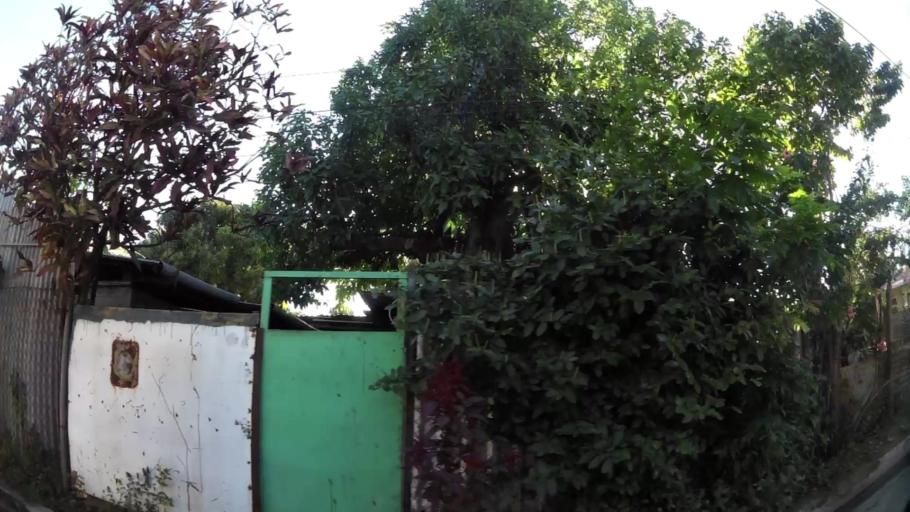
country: SV
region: Sonsonate
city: Sonsonate
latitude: 13.7132
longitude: -89.7159
